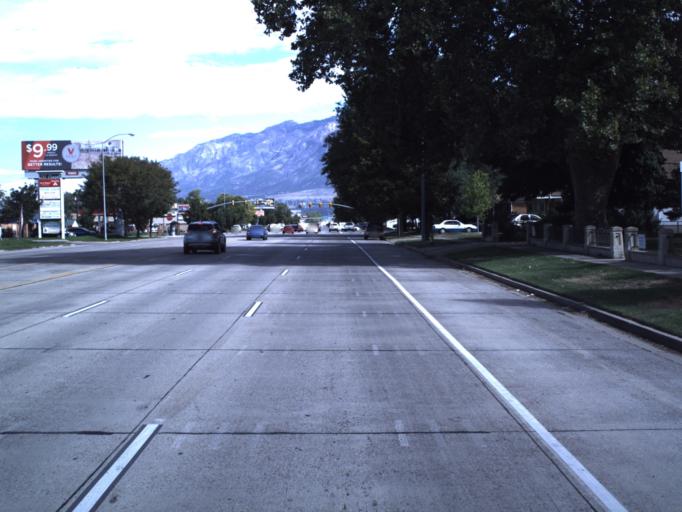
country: US
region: Utah
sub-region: Weber County
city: Ogden
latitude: 41.2498
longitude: -111.9697
